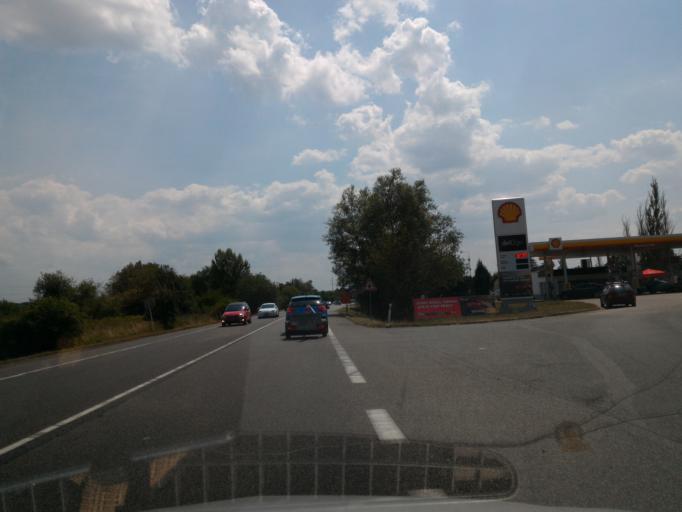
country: CZ
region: Central Bohemia
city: Cirkvice
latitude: 49.9706
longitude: 15.3090
